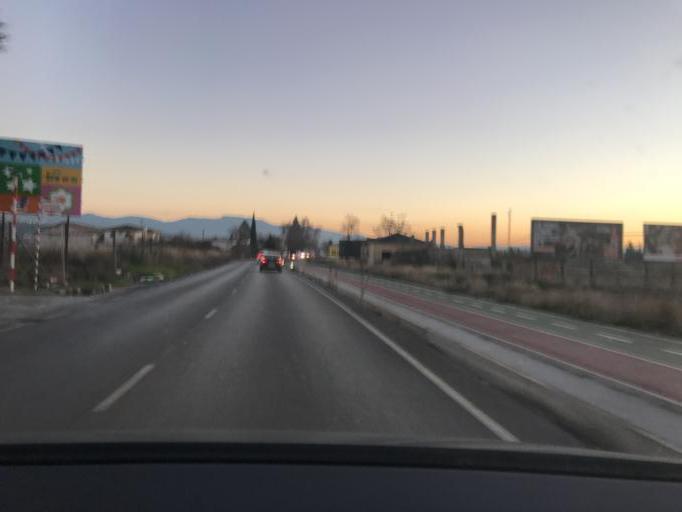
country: ES
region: Andalusia
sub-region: Provincia de Granada
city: Armilla
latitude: 37.1409
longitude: -3.6024
